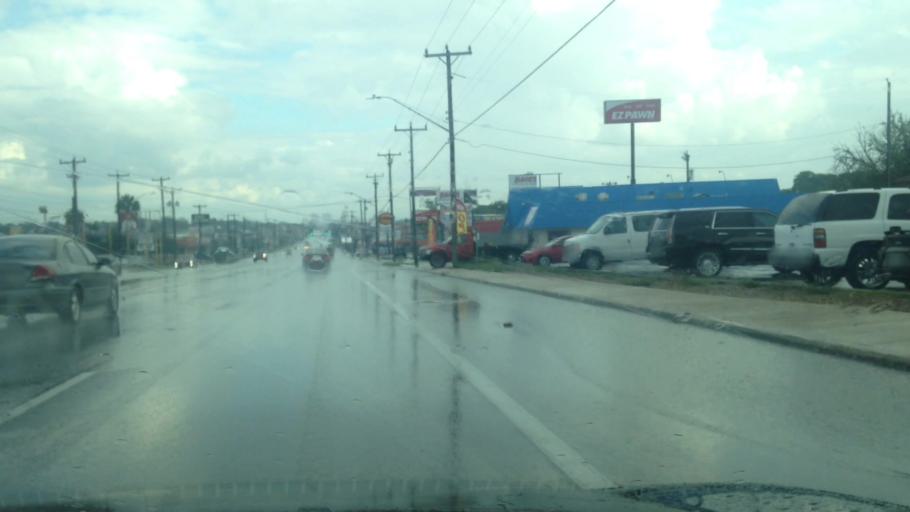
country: US
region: Texas
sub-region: Bexar County
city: Balcones Heights
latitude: 29.4830
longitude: -98.5445
